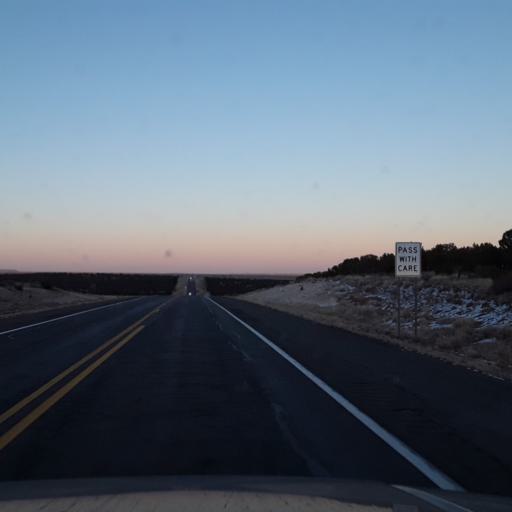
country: US
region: New Mexico
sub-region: Torrance County
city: Estancia
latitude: 34.5210
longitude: -105.3319
